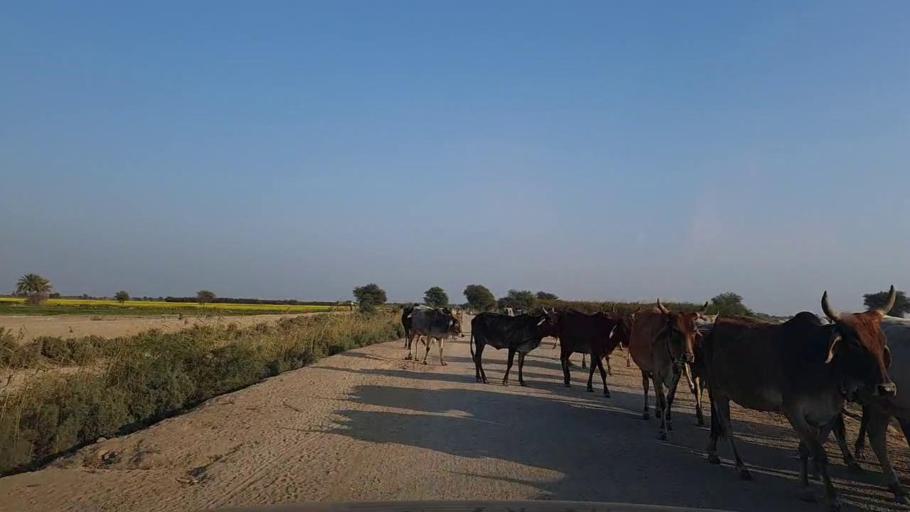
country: PK
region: Sindh
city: Tando Mittha Khan
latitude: 25.9392
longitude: 69.0822
